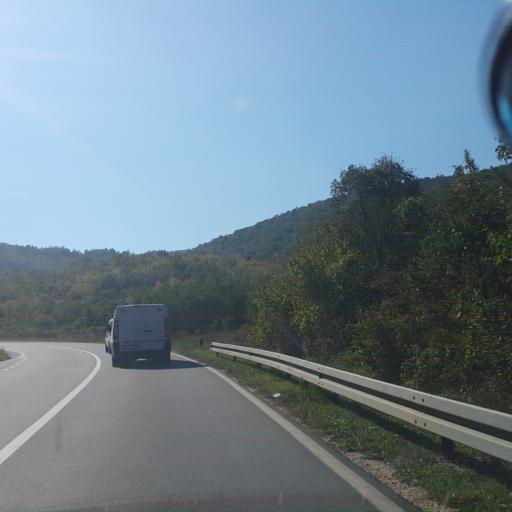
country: RS
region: Central Serbia
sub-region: Zajecarski Okrug
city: Knjazevac
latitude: 43.5390
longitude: 22.2287
